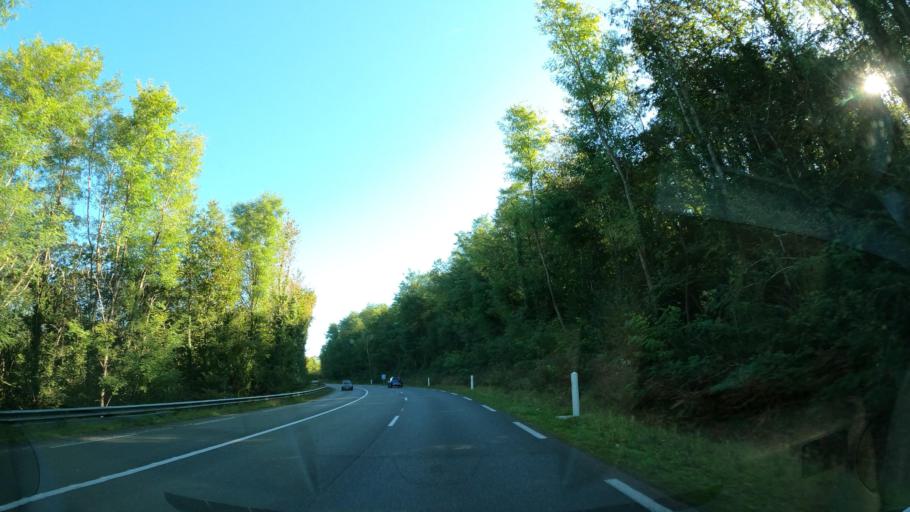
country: FR
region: Aquitaine
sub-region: Departement de la Dordogne
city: Vergt
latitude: 45.0642
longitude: 0.6817
